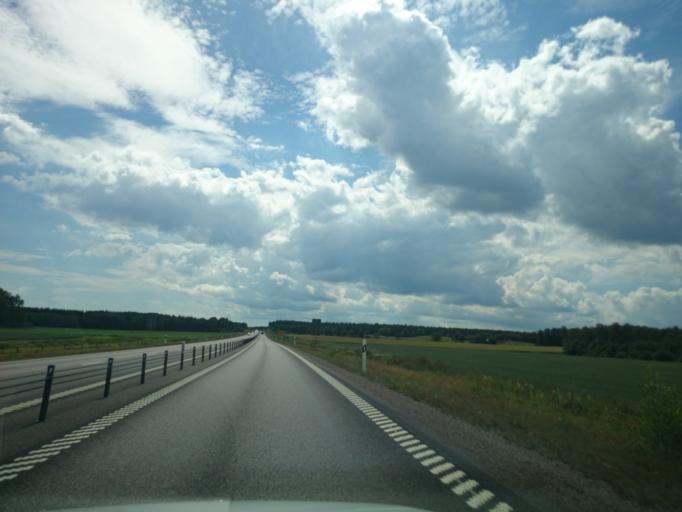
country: SE
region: Kalmar
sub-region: Kalmar Kommun
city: Ljungbyholm
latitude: 56.6085
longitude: 16.1374
